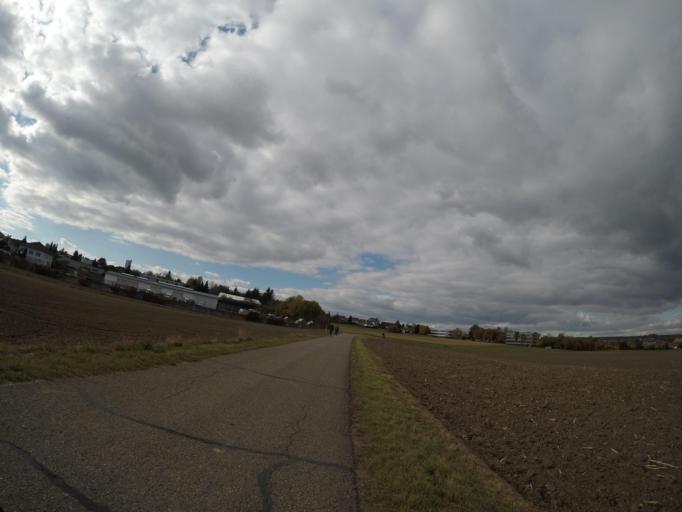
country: DE
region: Baden-Wuerttemberg
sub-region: Tuebingen Region
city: Munderkingen
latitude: 48.2271
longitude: 9.6517
